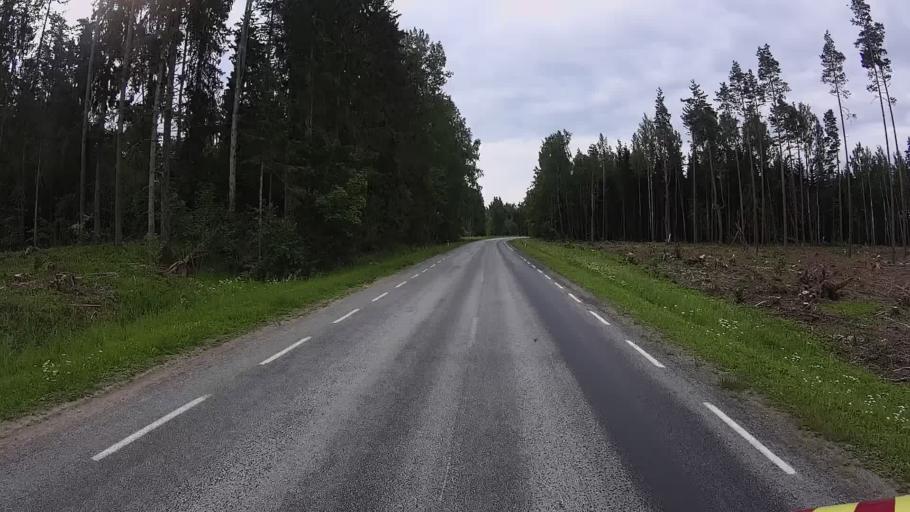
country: EE
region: Viljandimaa
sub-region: Karksi vald
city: Karksi-Nuia
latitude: 58.2202
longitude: 25.6172
